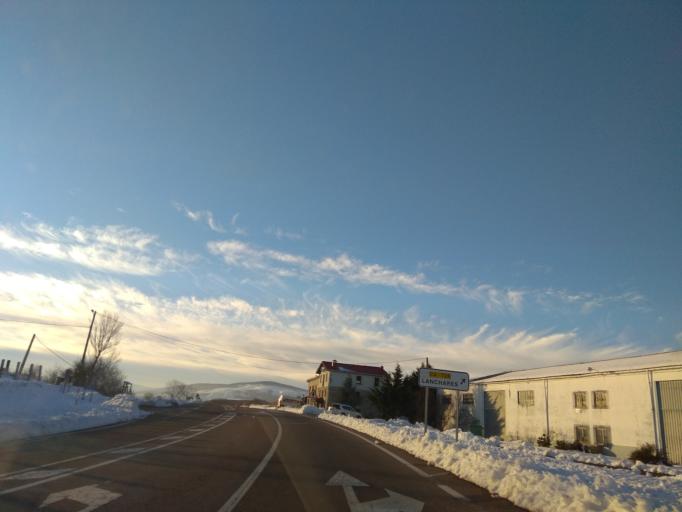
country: ES
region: Castille and Leon
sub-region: Provincia de Burgos
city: Arija
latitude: 43.0262
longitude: -3.9671
